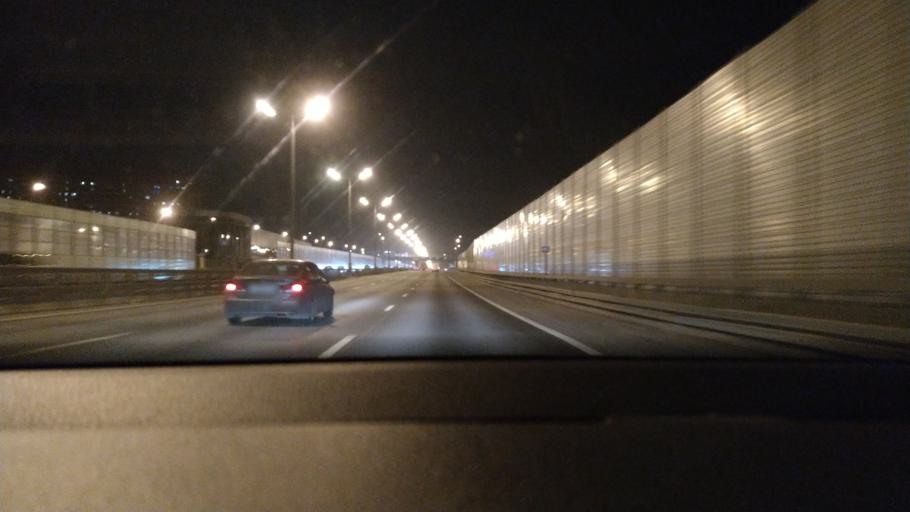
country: RU
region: Moskovskaya
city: Aprelevka
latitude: 55.5371
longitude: 37.0749
